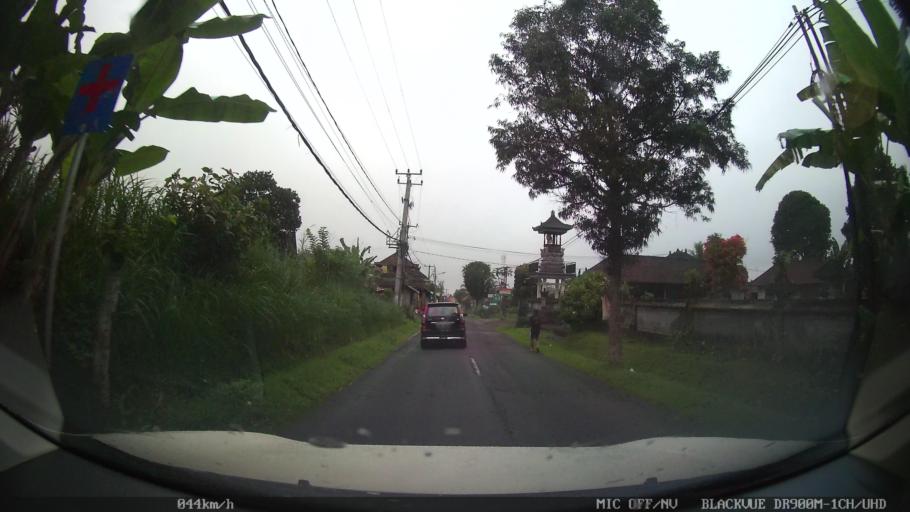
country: ID
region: Bali
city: Banjar Taro Kelod
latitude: -8.3762
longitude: 115.2675
